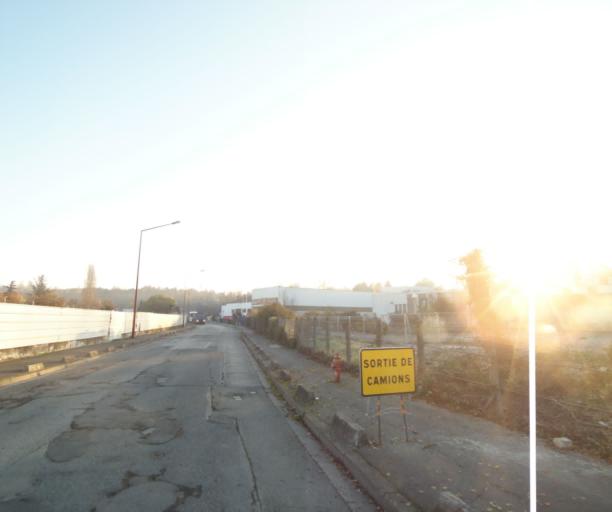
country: FR
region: Ile-de-France
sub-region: Departement du Val-d'Oise
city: Gonesse
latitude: 48.9851
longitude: 2.4561
